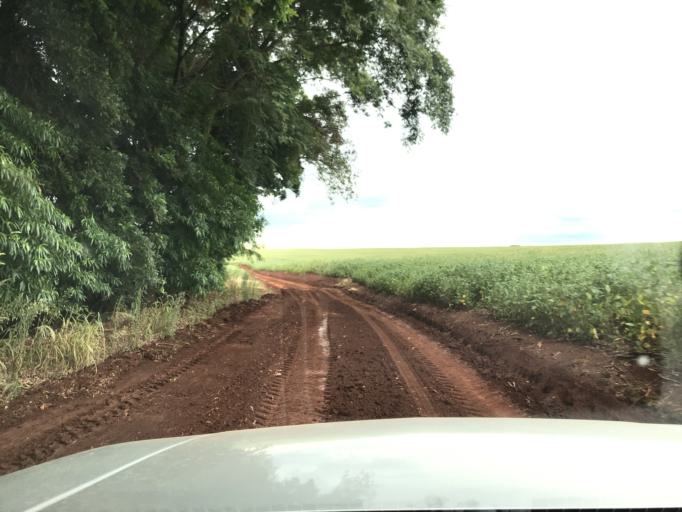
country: BR
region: Parana
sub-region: Palotina
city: Palotina
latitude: -24.2714
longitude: -53.7727
